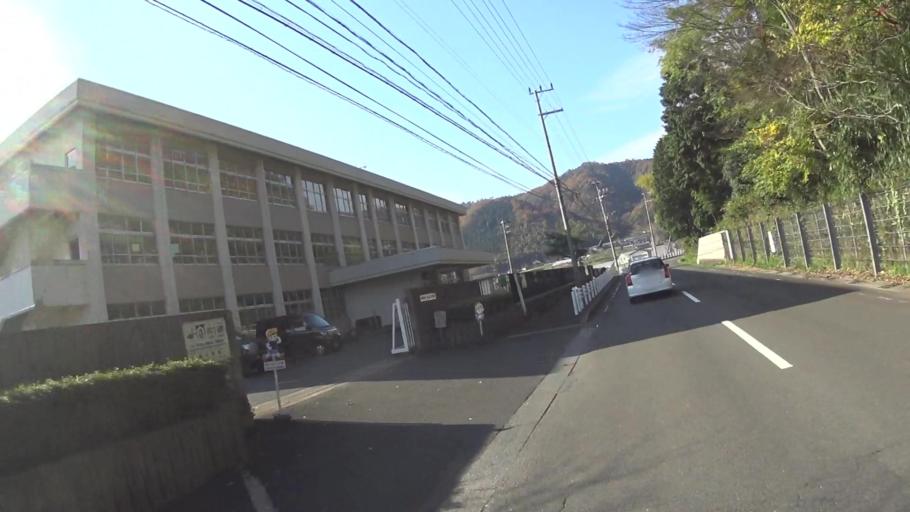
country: JP
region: Kyoto
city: Maizuru
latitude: 35.5178
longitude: 135.3966
